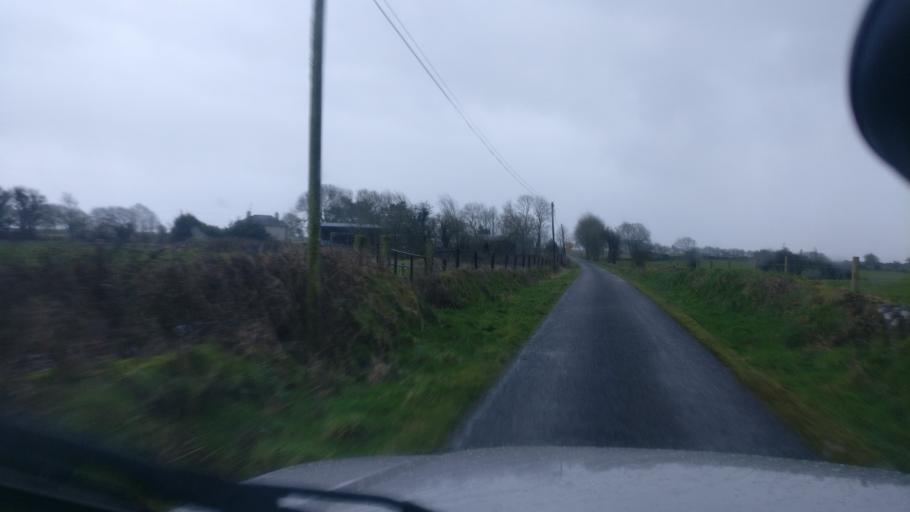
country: IE
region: Connaught
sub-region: County Galway
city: Loughrea
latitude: 53.2346
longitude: -8.4224
